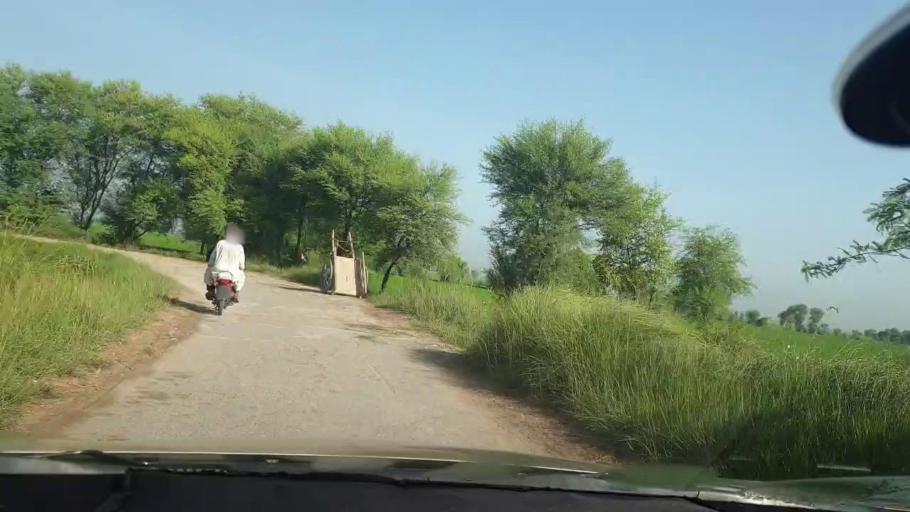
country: PK
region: Sindh
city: Kambar
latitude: 27.6604
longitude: 68.0222
